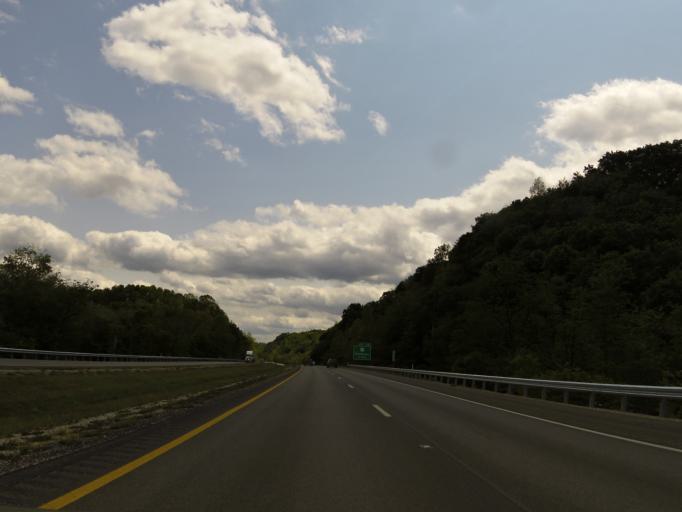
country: US
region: West Virginia
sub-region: Kanawha County
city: Sissonville
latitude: 38.6276
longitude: -81.6470
